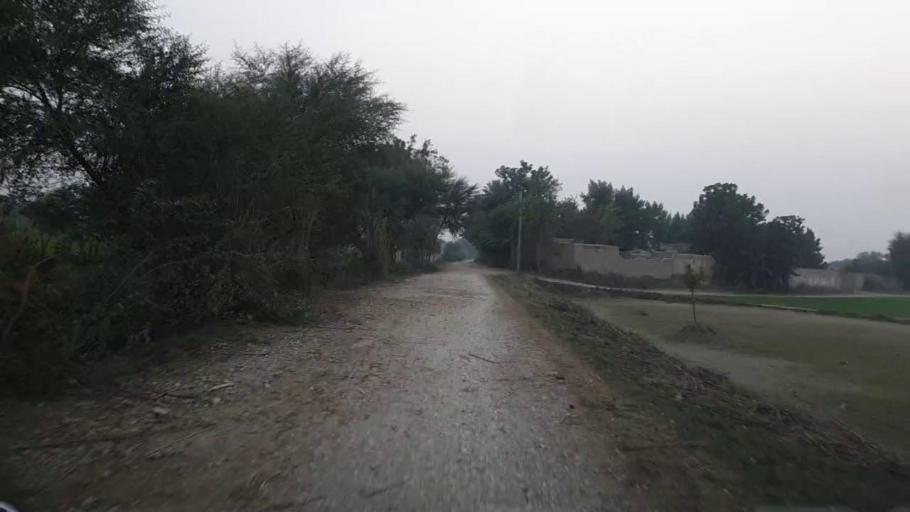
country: PK
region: Sindh
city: Kandiari
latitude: 26.9567
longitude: 68.4577
